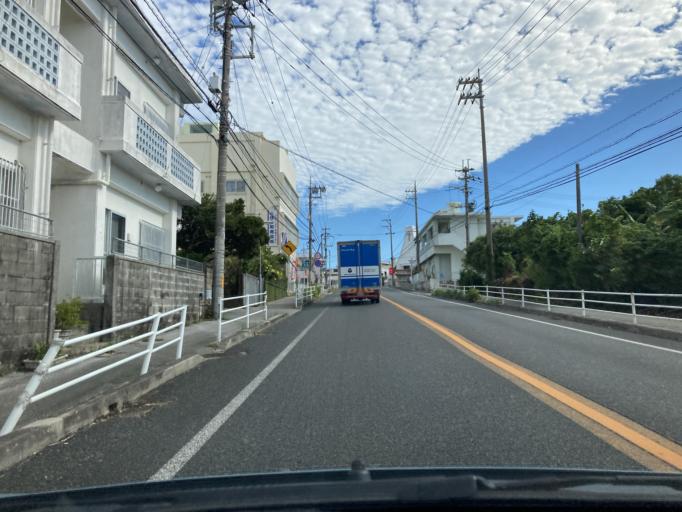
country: JP
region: Okinawa
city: Ishikawa
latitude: 26.4053
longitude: 127.7286
